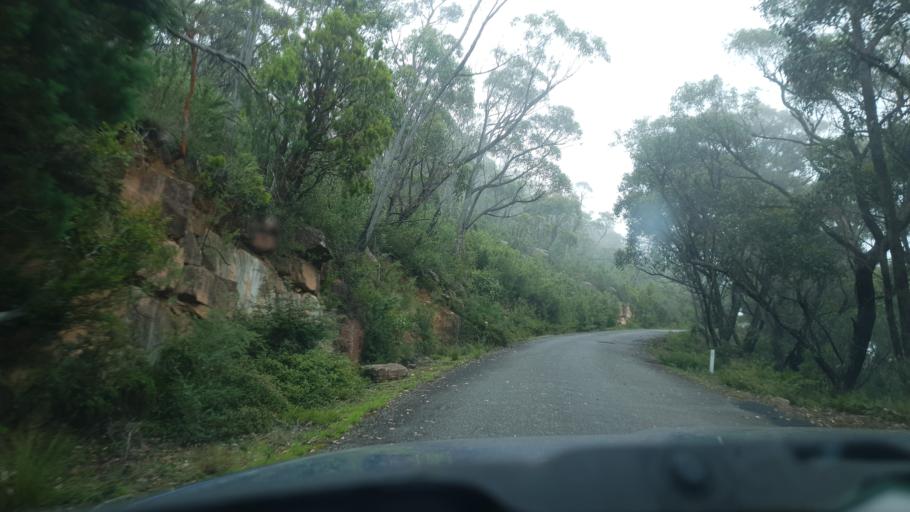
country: AU
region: Victoria
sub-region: Northern Grampians
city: Stawell
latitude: -37.2780
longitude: 142.5839
